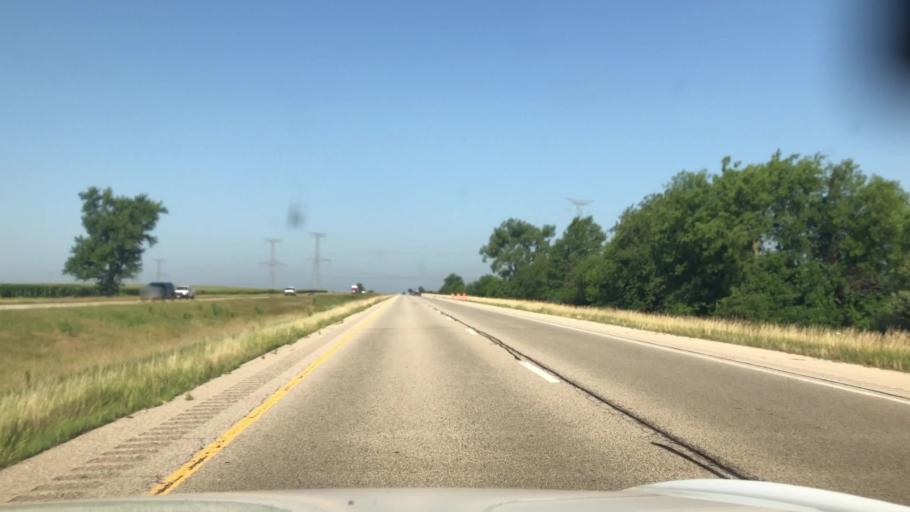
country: US
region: Illinois
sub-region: Tazewell County
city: Morton
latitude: 40.6223
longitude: -89.3830
